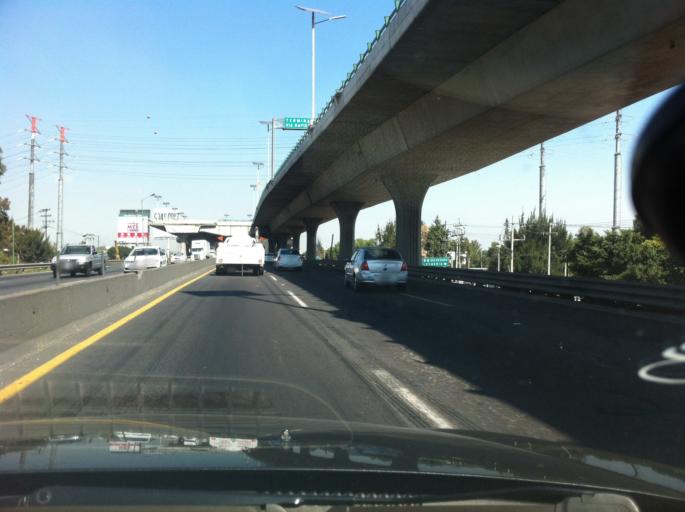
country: MX
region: Mexico
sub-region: Tultitlan
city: Buenavista
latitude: 19.6155
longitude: -99.1909
